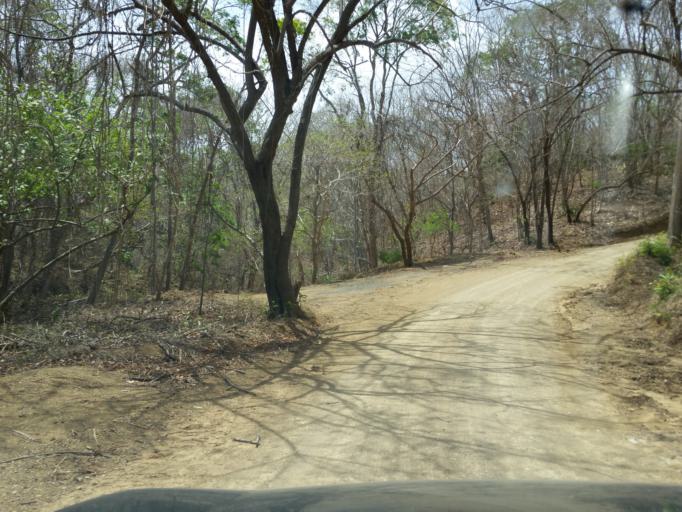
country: NI
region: Rivas
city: Tola
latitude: 11.4304
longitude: -86.0699
